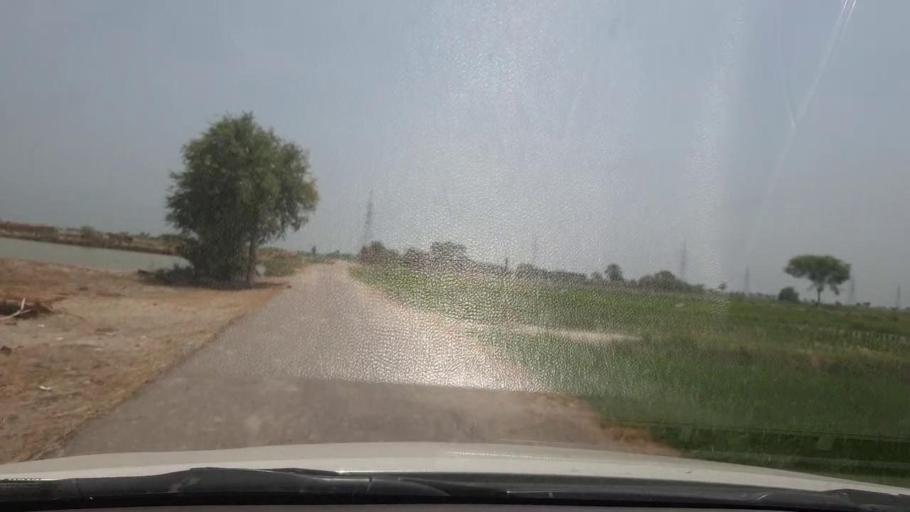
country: PK
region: Sindh
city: Shikarpur
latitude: 28.0951
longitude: 68.6130
